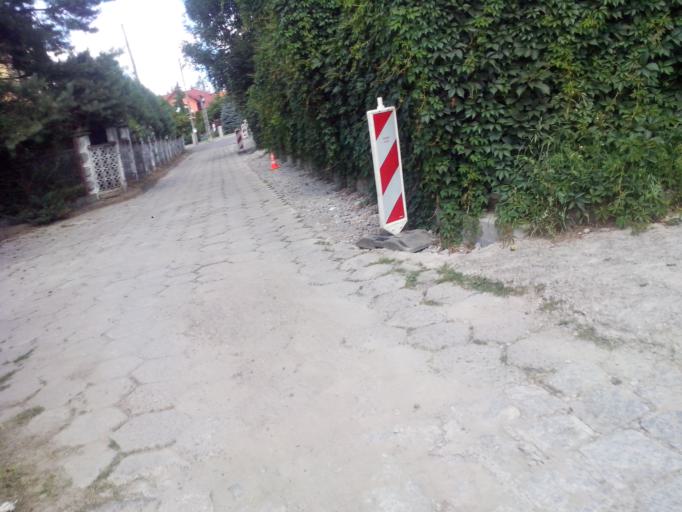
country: PL
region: Subcarpathian Voivodeship
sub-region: Powiat strzyzowski
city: Strzyzow
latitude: 49.8675
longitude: 21.7836
